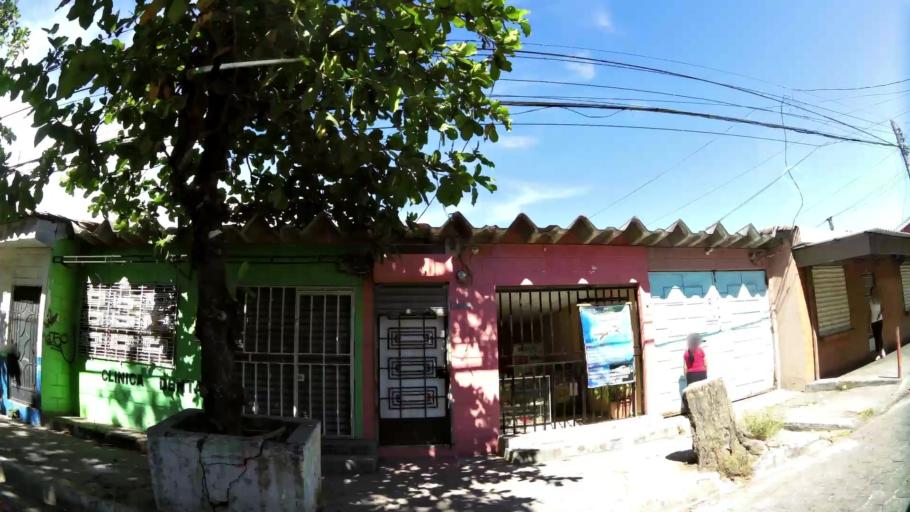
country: SV
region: San Salvador
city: Apopa
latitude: 13.8032
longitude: -89.1779
